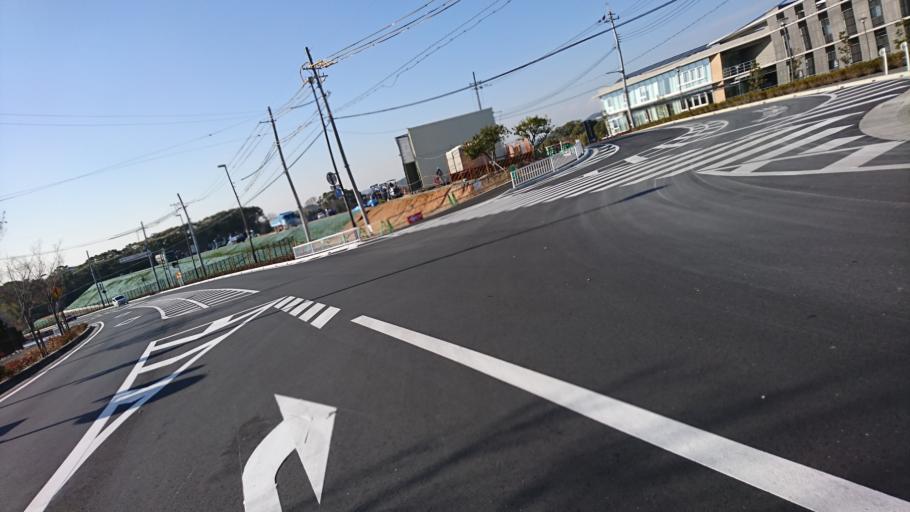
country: JP
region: Hyogo
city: Kakogawacho-honmachi
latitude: 34.7759
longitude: 134.8829
